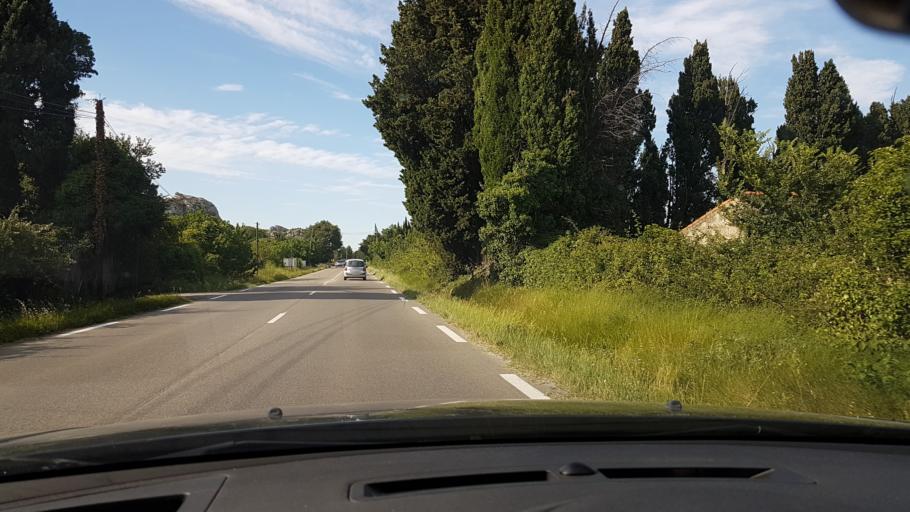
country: FR
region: Provence-Alpes-Cote d'Azur
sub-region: Departement des Bouches-du-Rhone
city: Graveson
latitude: 43.8700
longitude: 4.7712
